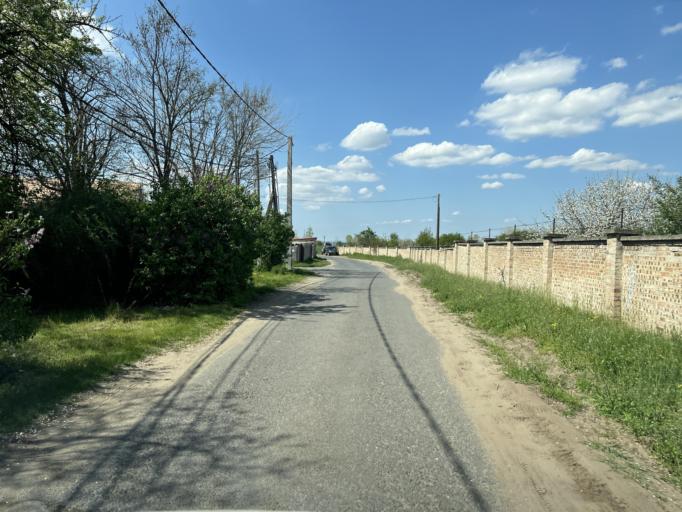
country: HU
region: Pest
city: Gyal
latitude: 47.3856
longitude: 19.2446
